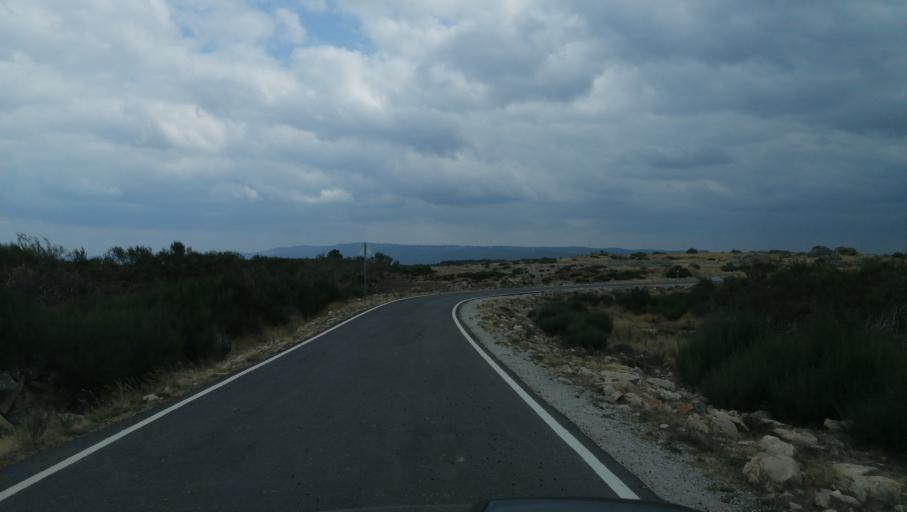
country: PT
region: Vila Real
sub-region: Vila Pouca de Aguiar
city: Vila Pouca de Aguiar
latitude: 41.5462
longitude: -7.6699
